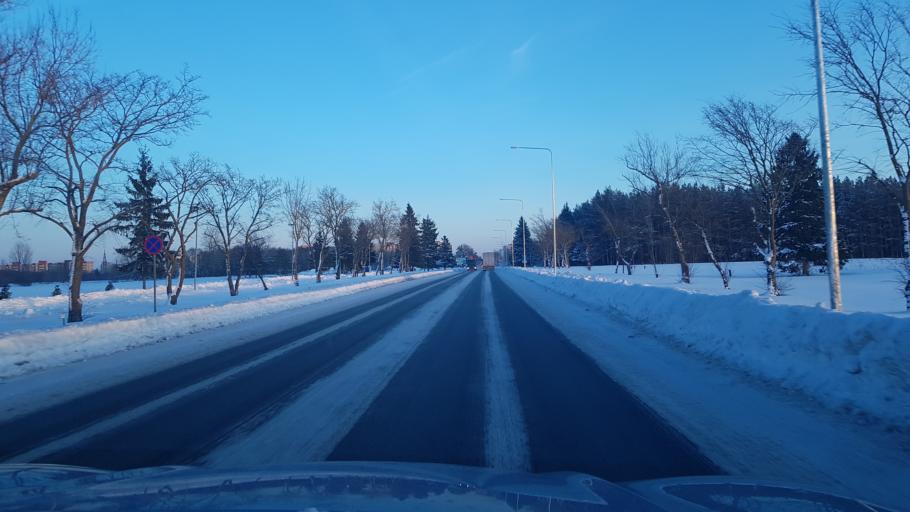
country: EE
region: Ida-Virumaa
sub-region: Narva linn
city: Narva
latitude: 59.3865
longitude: 28.1492
